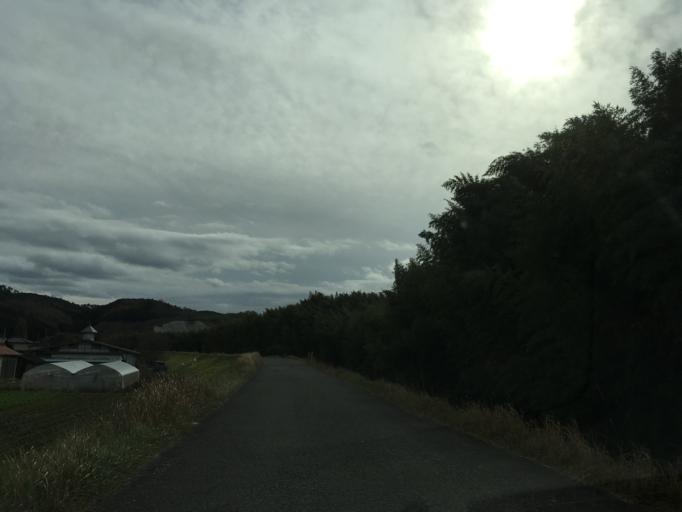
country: JP
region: Iwate
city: Ichinoseki
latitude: 38.7576
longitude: 141.2781
